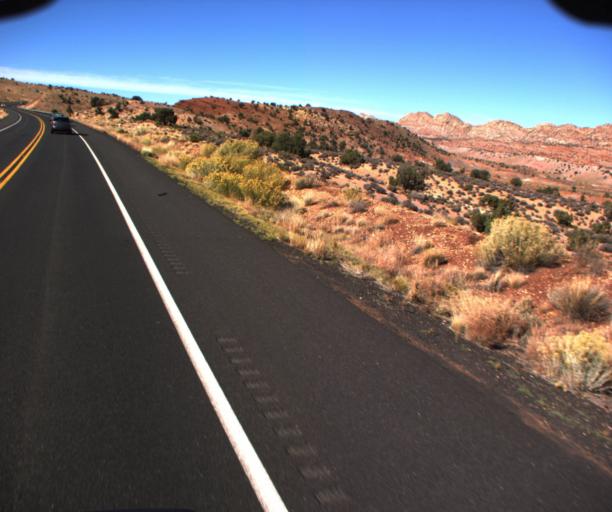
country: US
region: Arizona
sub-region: Coconino County
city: Tuba City
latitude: 36.3421
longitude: -111.4987
